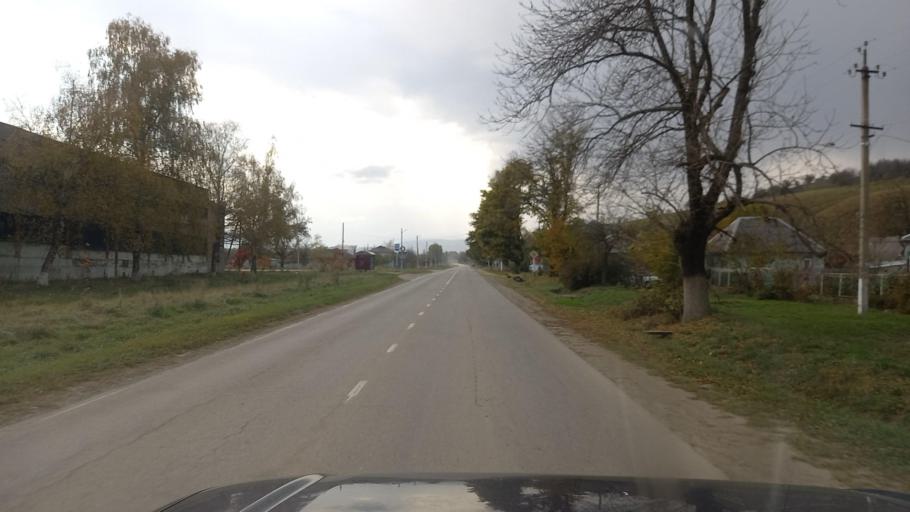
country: RU
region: Krasnodarskiy
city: Psebay
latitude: 44.1396
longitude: 40.8204
